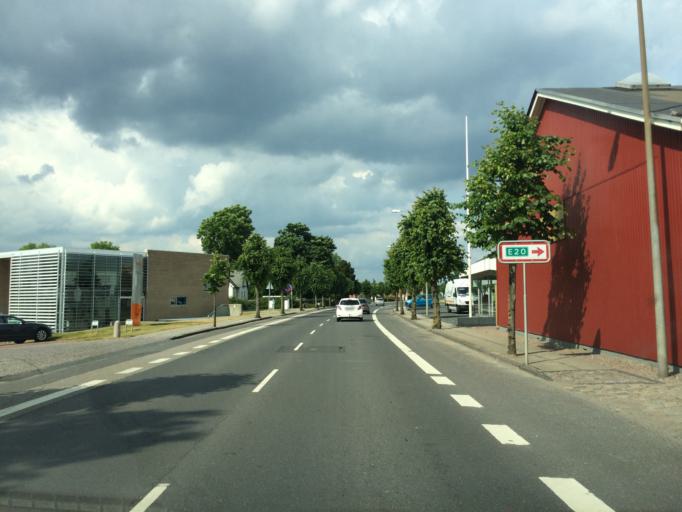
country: DK
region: South Denmark
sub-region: Middelfart Kommune
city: Middelfart
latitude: 55.5067
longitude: 9.7514
